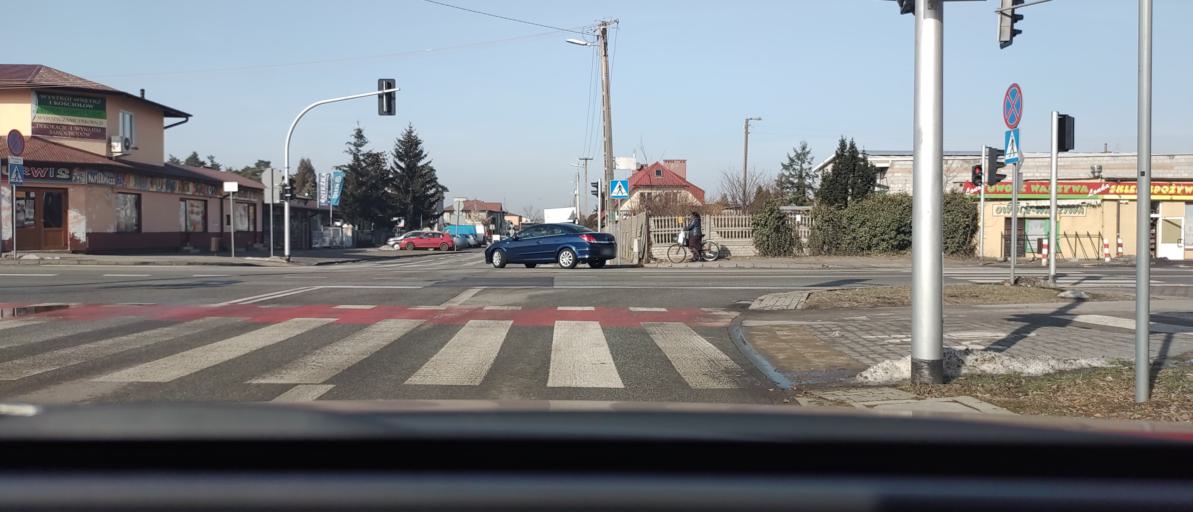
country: PL
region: Masovian Voivodeship
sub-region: Powiat bialobrzeski
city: Bialobrzegi
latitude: 51.6439
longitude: 20.9510
